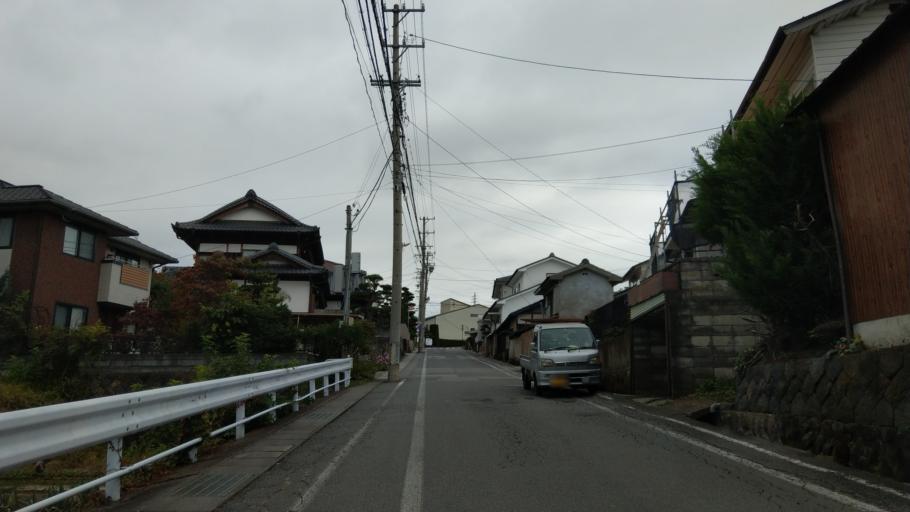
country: JP
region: Nagano
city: Komoro
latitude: 36.3317
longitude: 138.4256
